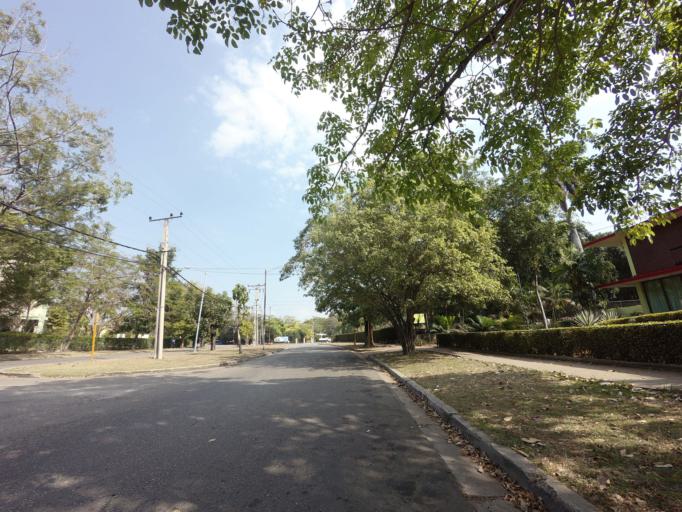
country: CU
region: La Habana
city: Cerro
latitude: 23.0797
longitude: -82.4461
